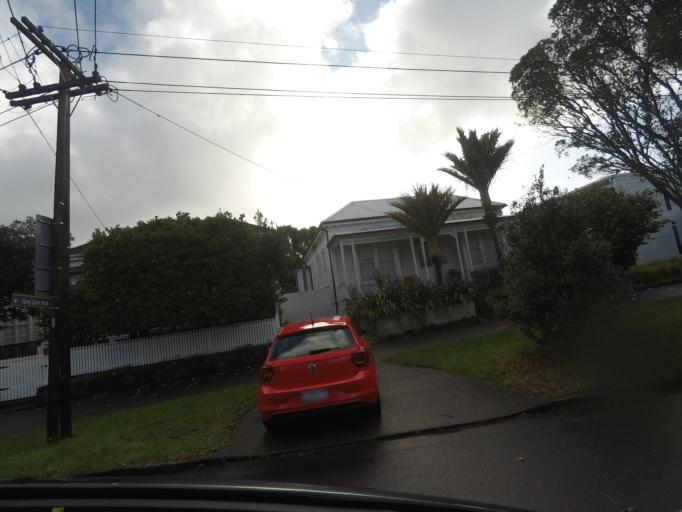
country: NZ
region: Auckland
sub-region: Auckland
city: Auckland
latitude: -36.8571
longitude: 174.7410
